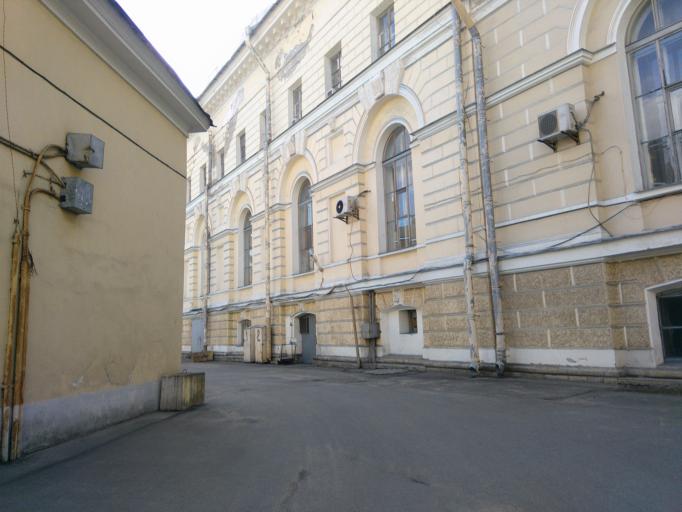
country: RU
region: St.-Petersburg
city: Saint Petersburg
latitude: 59.9445
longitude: 30.3009
